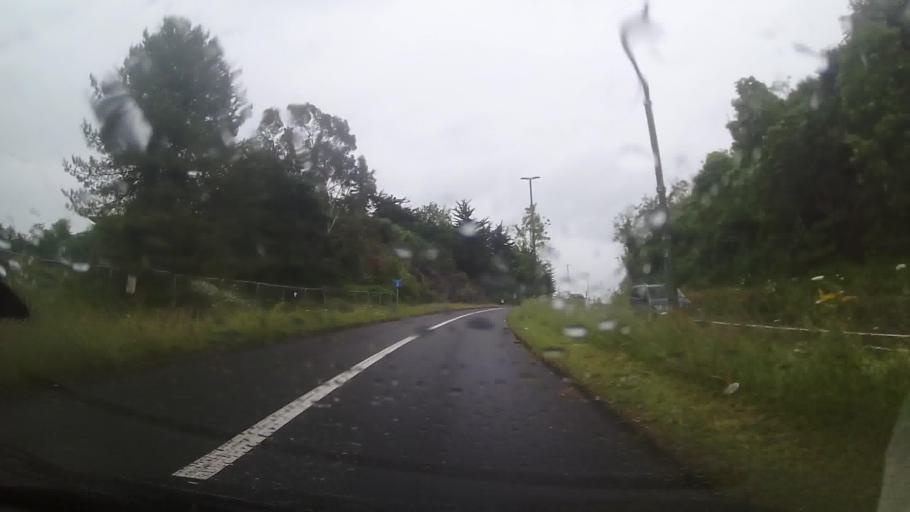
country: GB
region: England
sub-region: Borough of Torbay
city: Paignton
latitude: 50.4129
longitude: -3.5606
